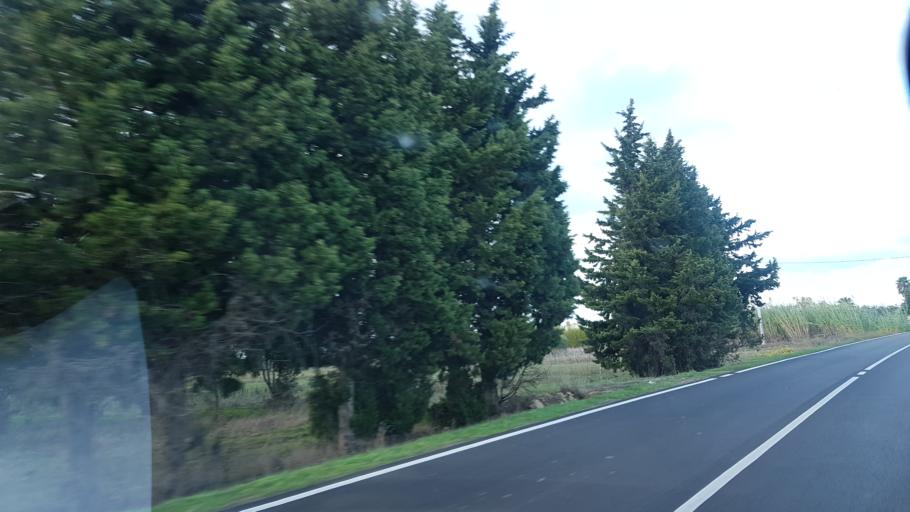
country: IT
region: Apulia
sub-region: Provincia di Brindisi
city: San Pietro Vernotico
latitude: 40.5104
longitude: 18.0094
